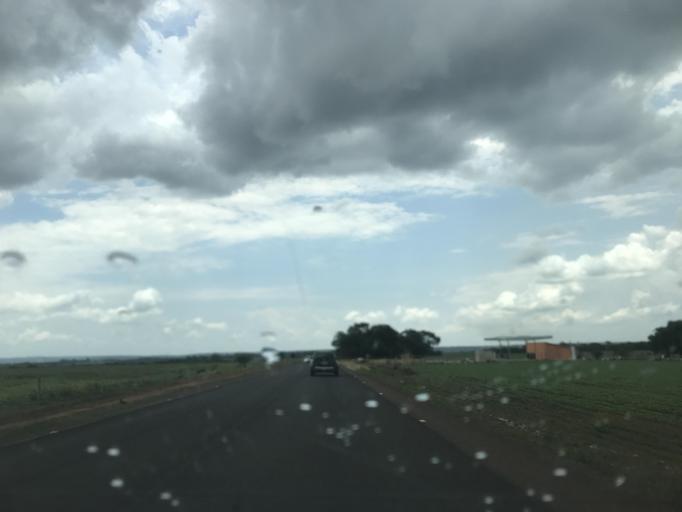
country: BR
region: Goias
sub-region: Vianopolis
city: Vianopolis
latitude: -16.9084
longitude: -48.5530
